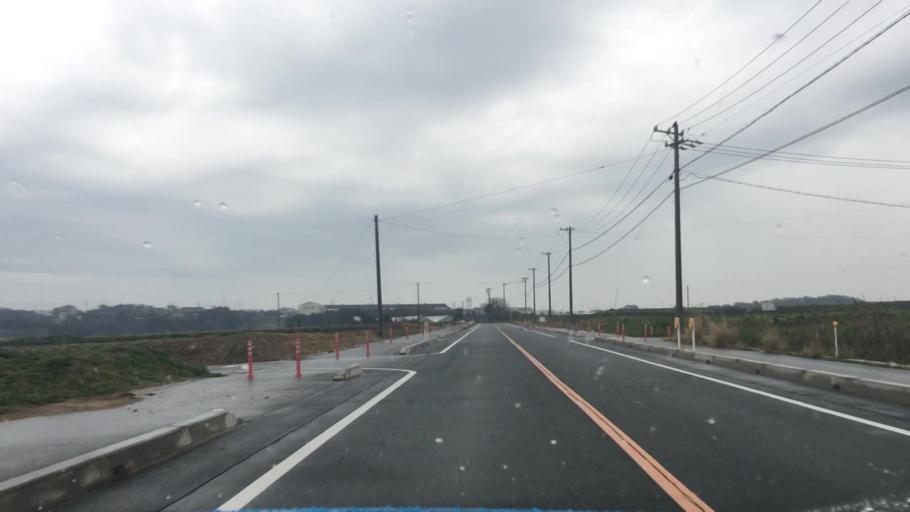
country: JP
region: Aichi
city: Toyohashi
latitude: 34.6722
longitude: 137.3903
